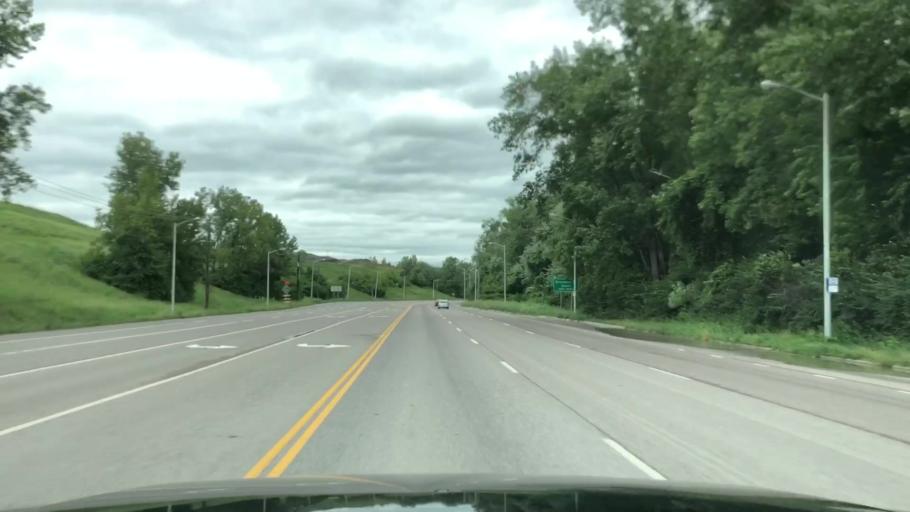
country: US
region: Missouri
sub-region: Saint Charles County
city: Saint Charles
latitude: 38.7481
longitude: -90.4634
